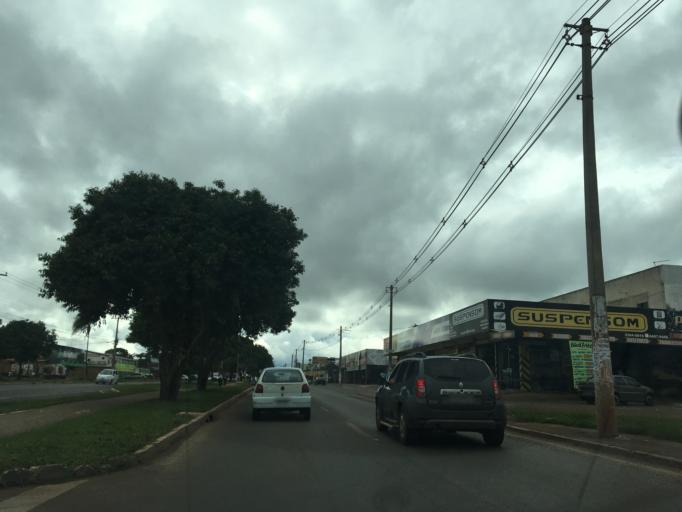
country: BR
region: Federal District
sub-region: Brasilia
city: Brasilia
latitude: -16.0040
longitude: -47.9895
